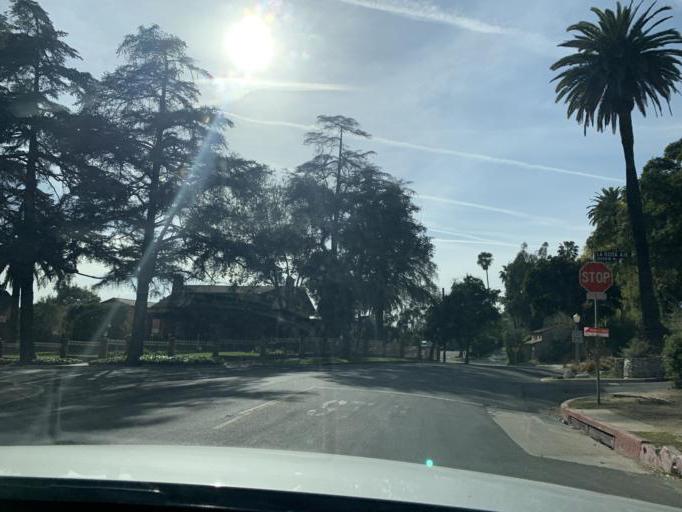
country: US
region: California
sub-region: Los Angeles County
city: Glendale
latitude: 34.1436
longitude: -118.2048
